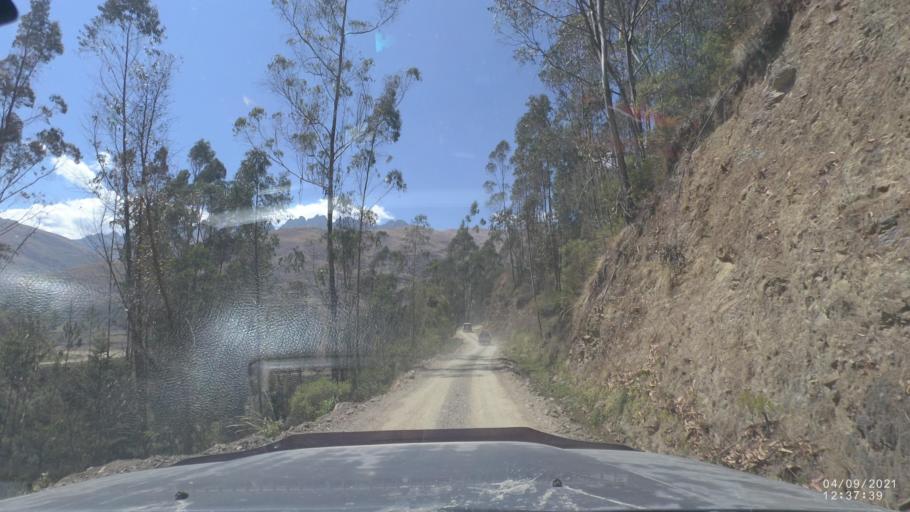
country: BO
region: Cochabamba
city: Colchani
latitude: -17.2273
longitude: -66.5046
